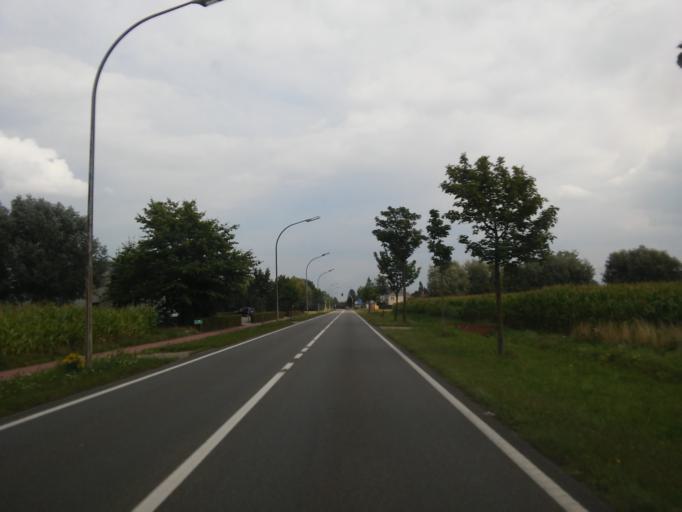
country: BE
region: Flanders
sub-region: Provincie Antwerpen
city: Puurs
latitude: 51.0523
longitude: 4.3024
